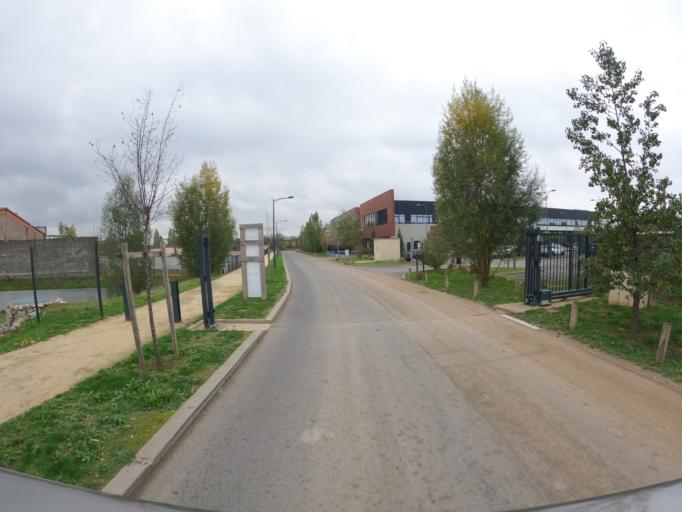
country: FR
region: Ile-de-France
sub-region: Departement du Val-de-Marne
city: Boissy-Saint-Leger
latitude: 48.7666
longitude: 2.4994
